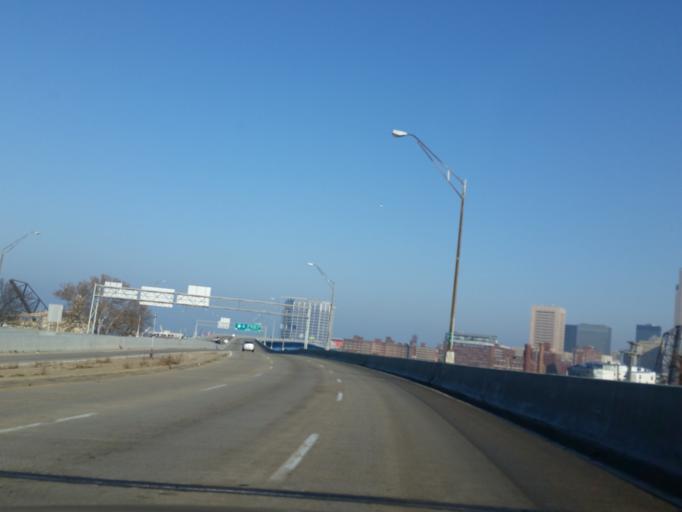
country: US
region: Ohio
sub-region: Cuyahoga County
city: Cleveland
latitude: 41.4920
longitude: -81.7089
